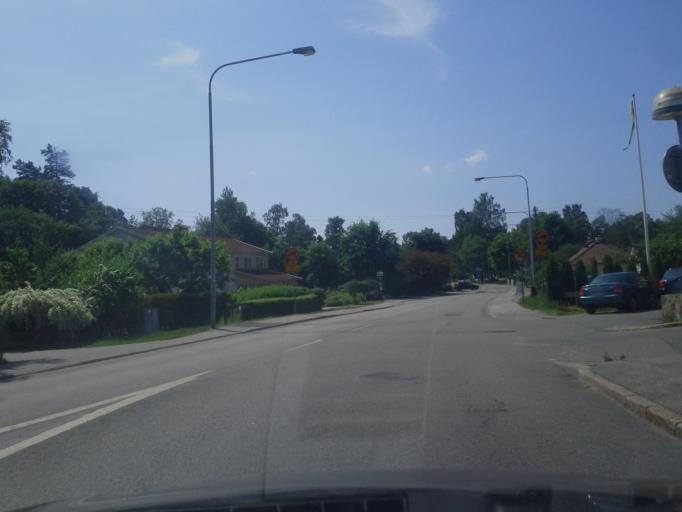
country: SE
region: Stockholm
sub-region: Huddinge Kommun
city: Huddinge
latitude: 59.2500
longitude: 17.9984
